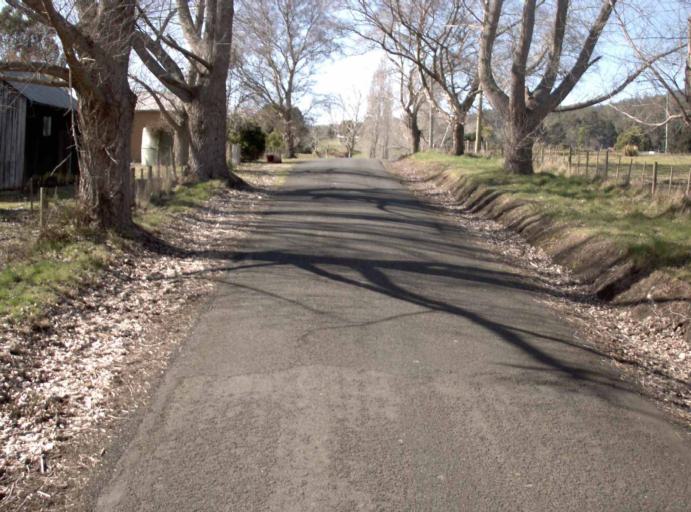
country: AU
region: Tasmania
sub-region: Launceston
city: Mayfield
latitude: -41.2894
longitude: 147.2082
